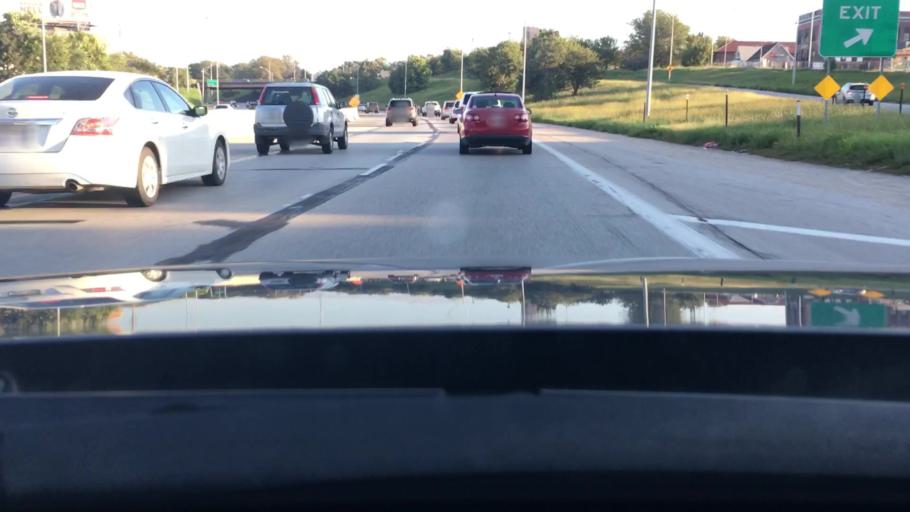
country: US
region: Nebraska
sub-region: Douglas County
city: Omaha
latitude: 41.2092
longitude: -95.9491
